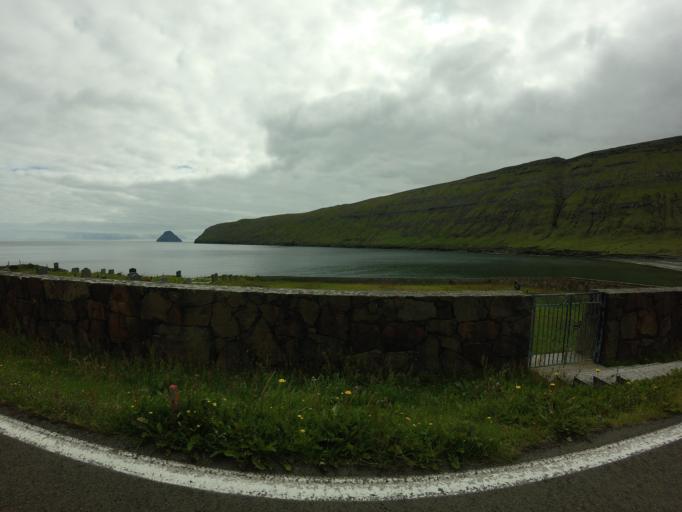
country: FO
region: Suduroy
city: Tvoroyri
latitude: 61.6299
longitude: -6.9301
